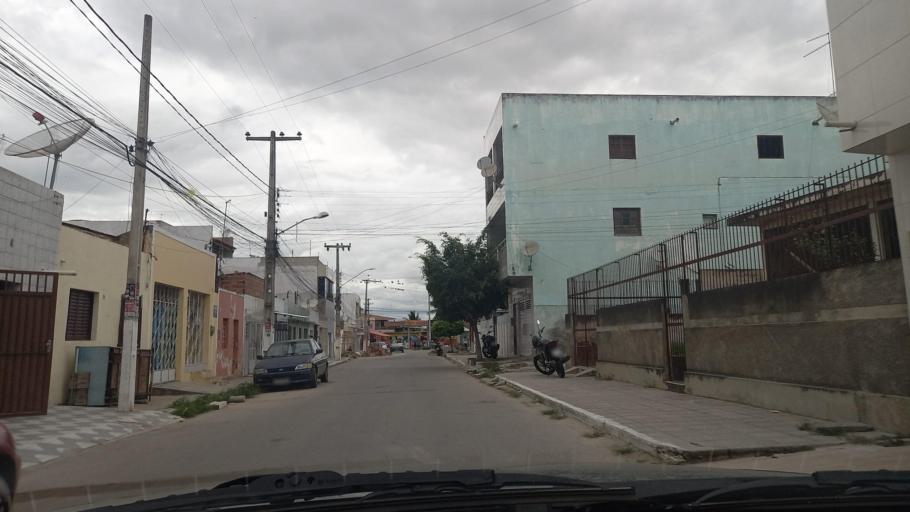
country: BR
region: Pernambuco
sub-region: Caruaru
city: Caruaru
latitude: -8.3306
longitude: -36.1364
